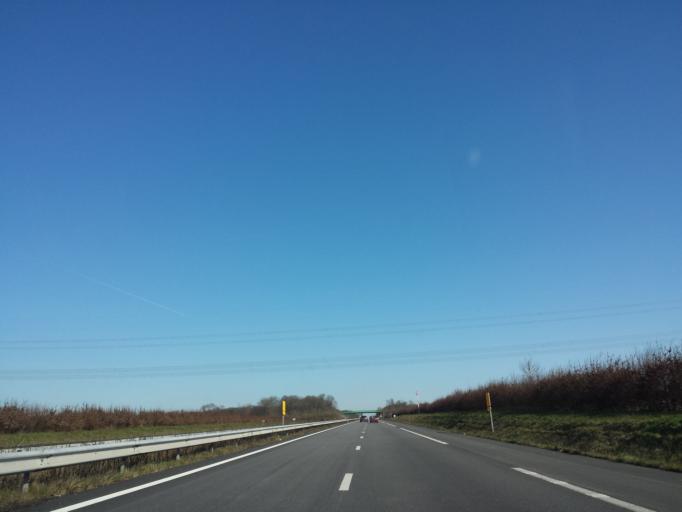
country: FR
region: Picardie
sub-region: Departement de l'Oise
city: Saint-Crepin-Ibouvillers
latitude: 49.3089
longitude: 2.0788
